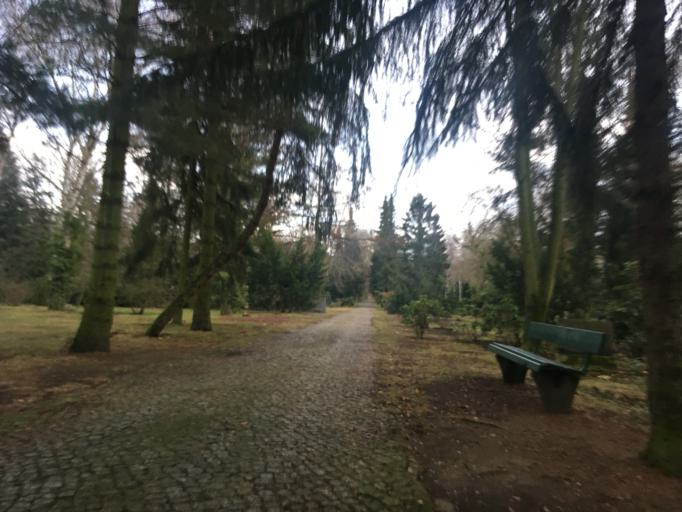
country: DE
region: Berlin
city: Reinickendorf
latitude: 52.5672
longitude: 13.3346
